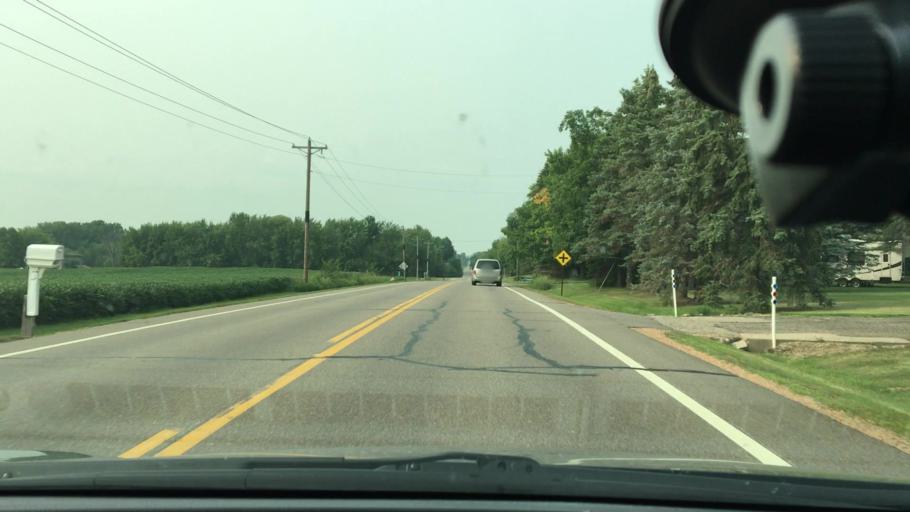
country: US
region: Minnesota
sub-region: Hennepin County
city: Champlin
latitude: 45.1646
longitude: -93.4621
